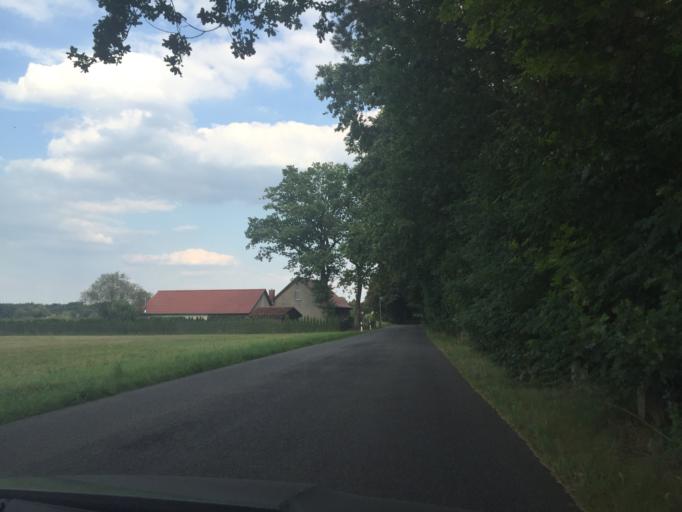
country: DE
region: Brandenburg
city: Spreenhagen
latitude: 52.3438
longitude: 13.8433
